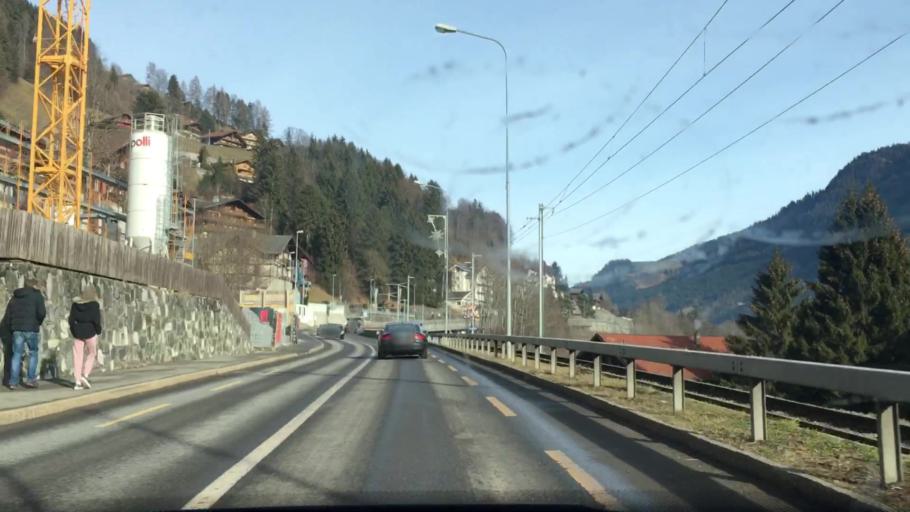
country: CH
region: Valais
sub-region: Monthey District
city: Champery
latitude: 46.1800
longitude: 6.8726
